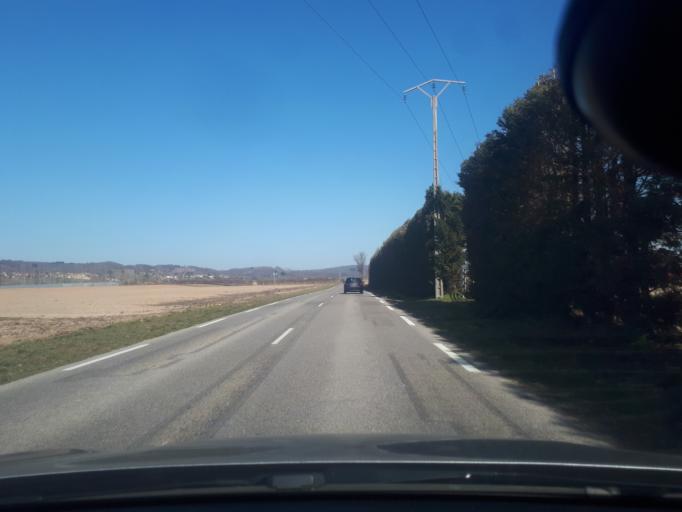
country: FR
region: Rhone-Alpes
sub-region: Departement de l'Isere
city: La Cote-Saint-Andre
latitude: 45.4183
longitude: 5.2642
